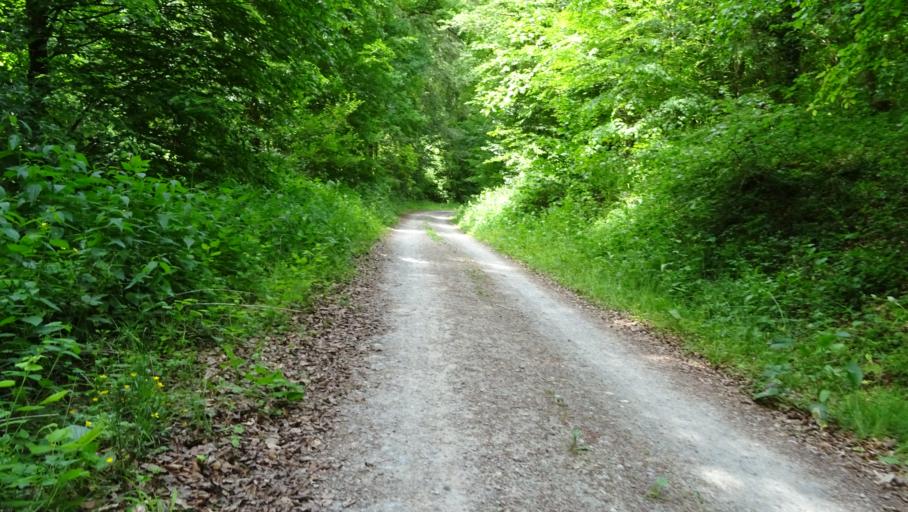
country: DE
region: Baden-Wuerttemberg
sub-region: Karlsruhe Region
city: Hassmersheim
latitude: 49.2967
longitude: 9.1584
